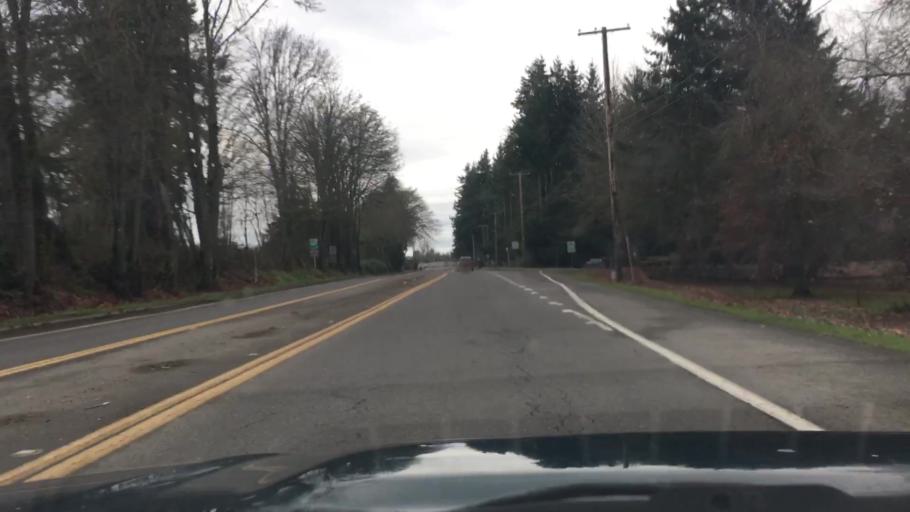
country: US
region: Oregon
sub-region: Lane County
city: Coburg
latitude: 44.1086
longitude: -123.0518
